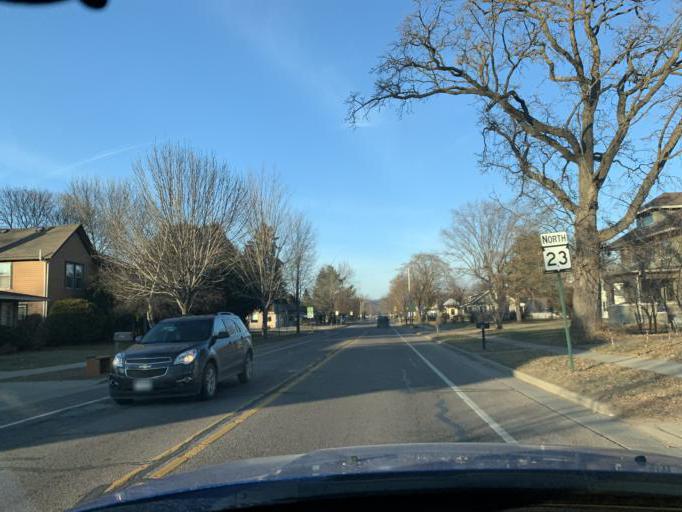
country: US
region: Wisconsin
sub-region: Sauk County
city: Spring Green
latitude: 43.1771
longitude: -90.0640
